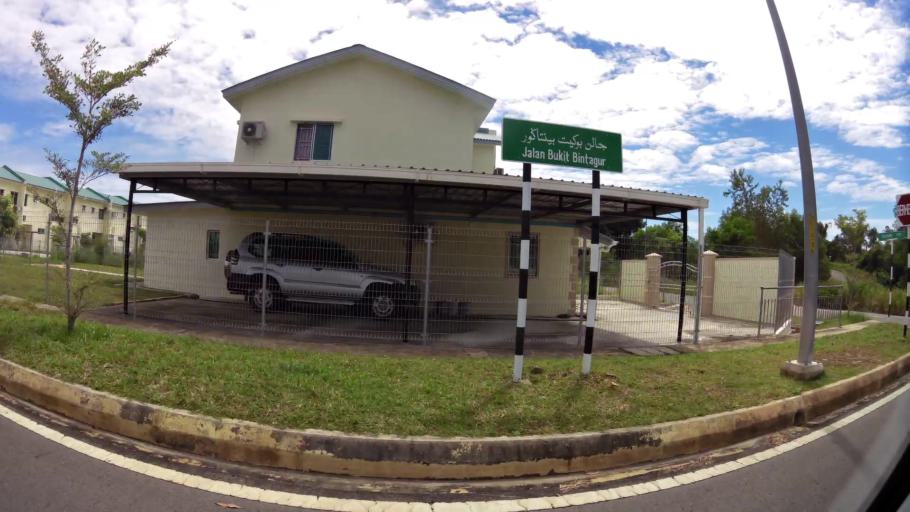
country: BN
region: Brunei and Muara
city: Bandar Seri Begawan
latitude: 4.9728
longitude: 115.0158
